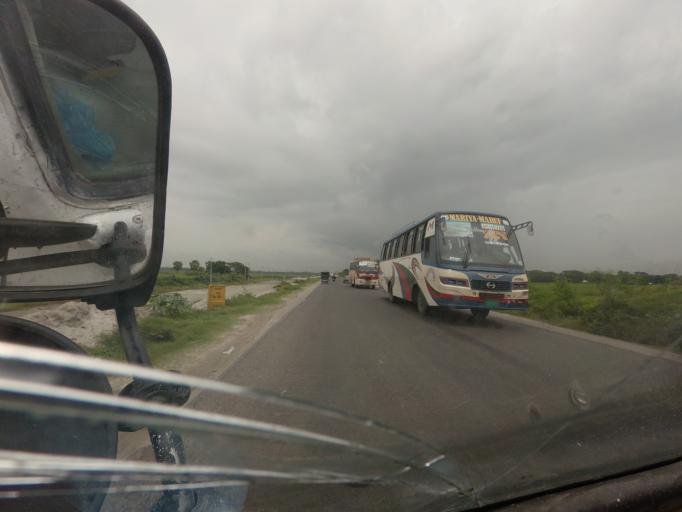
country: BD
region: Dhaka
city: Char Bhadrasan
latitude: 23.3701
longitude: 90.0466
